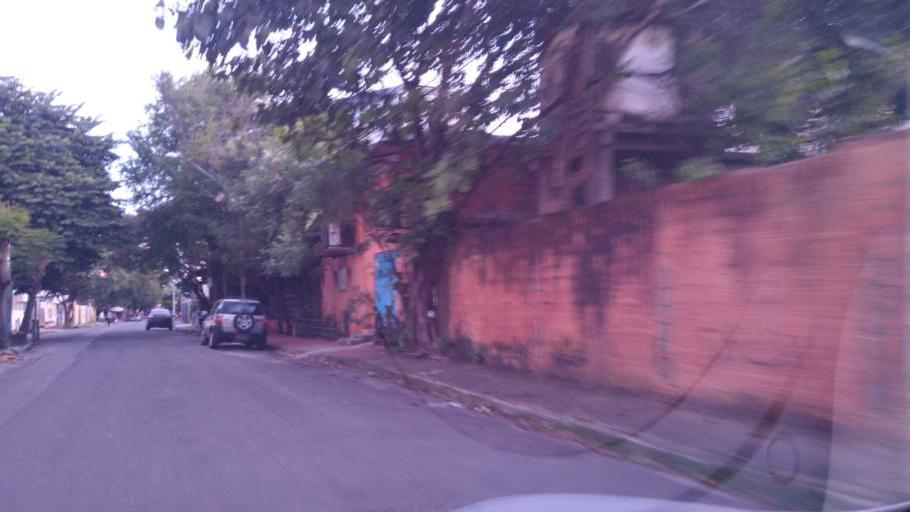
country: BR
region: Ceara
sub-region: Fortaleza
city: Fortaleza
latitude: -3.7302
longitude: -38.4884
